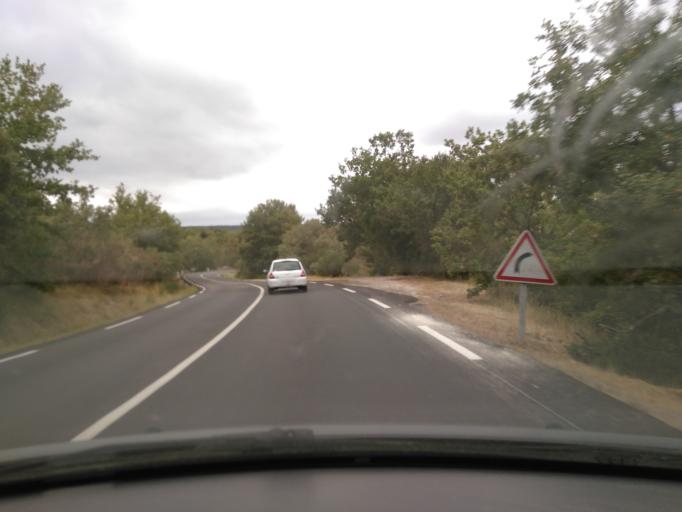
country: FR
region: Rhone-Alpes
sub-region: Departement de la Drome
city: Grignan
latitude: 44.4210
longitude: 4.8533
